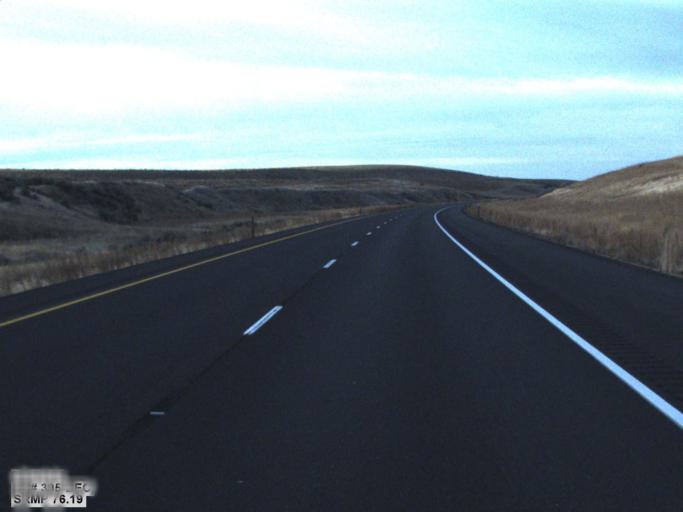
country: US
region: Washington
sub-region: Adams County
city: Ritzville
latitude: 46.8911
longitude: -118.6157
